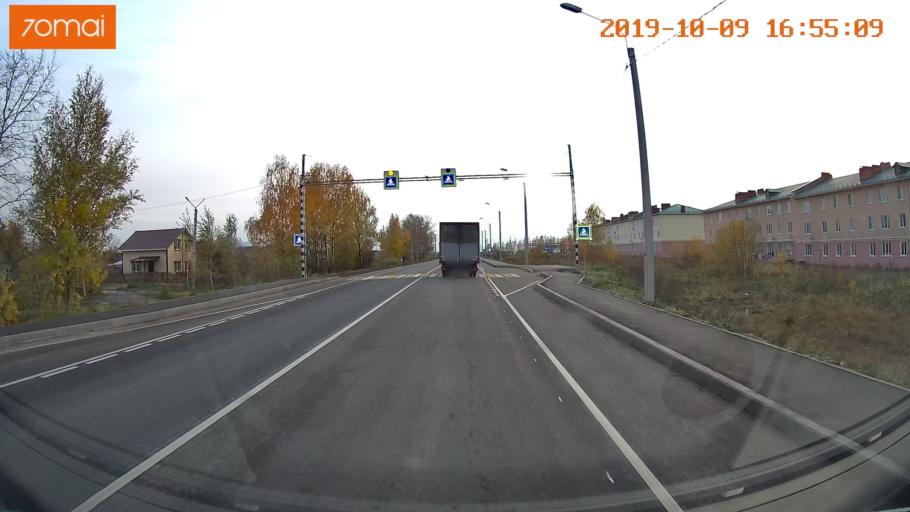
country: RU
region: Ivanovo
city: Privolzhsk
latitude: 57.3696
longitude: 41.2759
